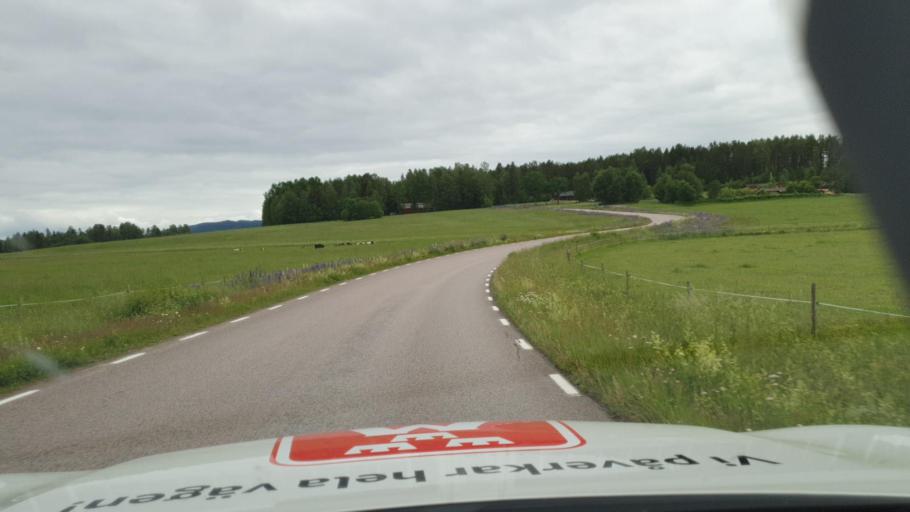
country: SE
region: Vaermland
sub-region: Sunne Kommun
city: Sunne
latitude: 59.7130
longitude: 13.2287
